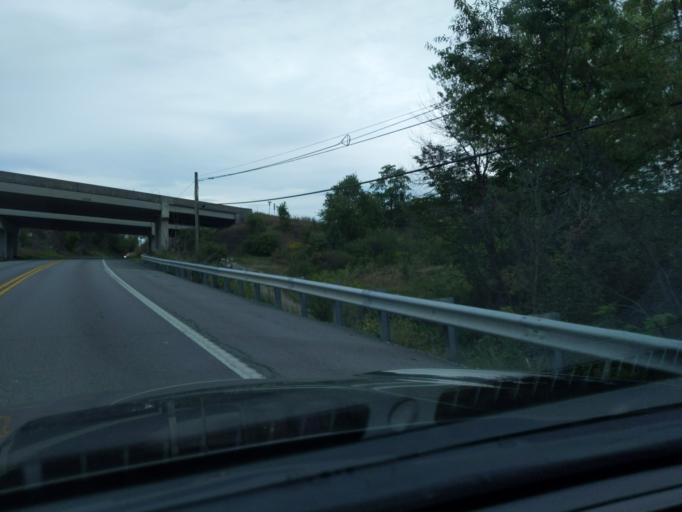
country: US
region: Pennsylvania
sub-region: Blair County
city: Duncansville
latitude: 40.3796
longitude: -78.4340
